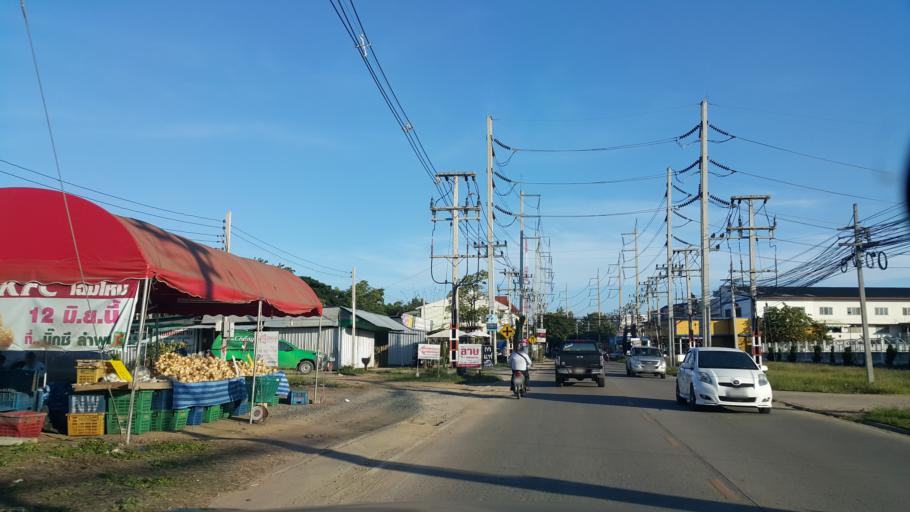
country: TH
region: Lamphun
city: Lamphun
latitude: 18.5912
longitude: 99.0385
